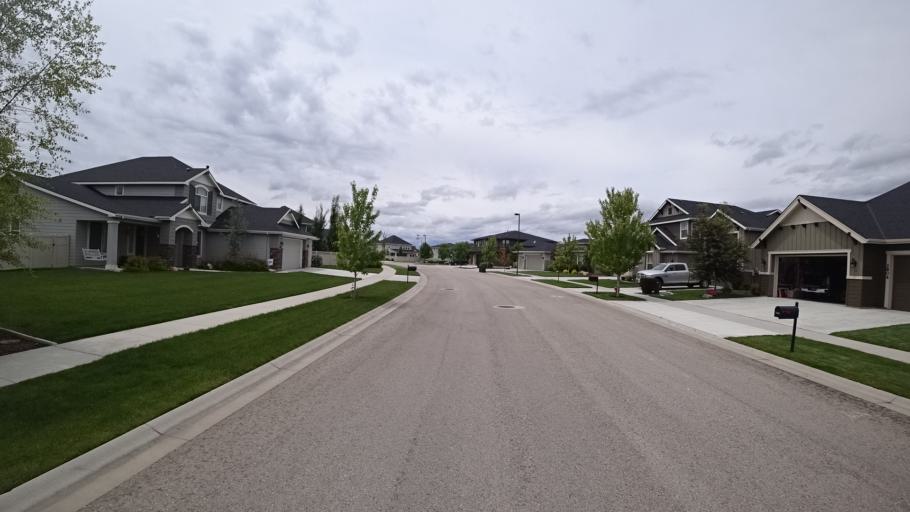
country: US
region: Idaho
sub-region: Ada County
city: Meridian
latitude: 43.6390
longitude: -116.4289
